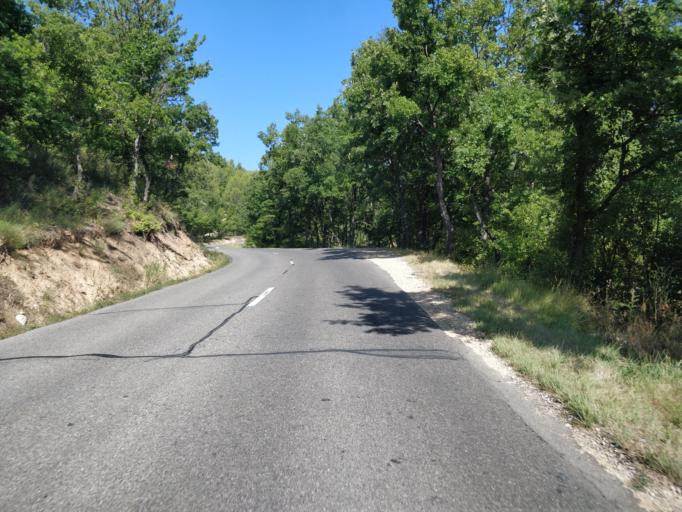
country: FR
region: Provence-Alpes-Cote d'Azur
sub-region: Departement des Alpes-de-Haute-Provence
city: Riez
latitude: 43.8489
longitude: 6.1980
